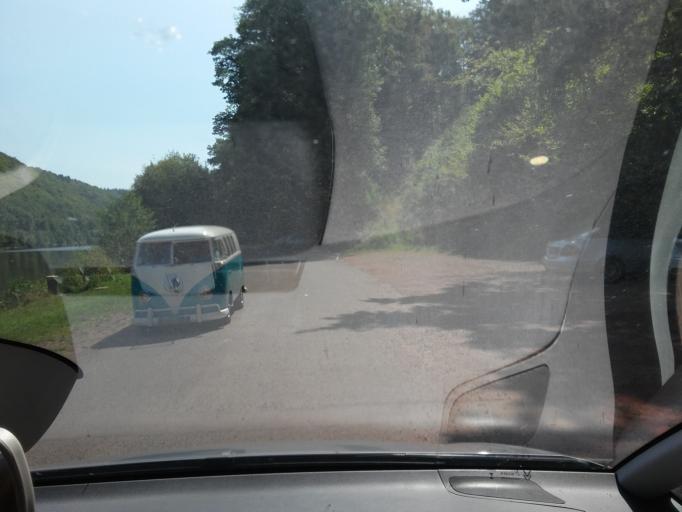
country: DE
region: Saarland
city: Orscholz
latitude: 49.4972
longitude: 6.5459
